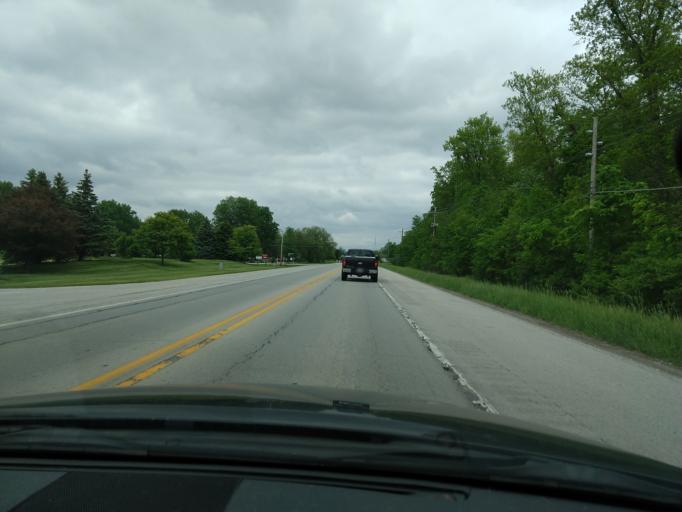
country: US
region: Indiana
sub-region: Hamilton County
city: Westfield
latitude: 40.0429
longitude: -86.1013
